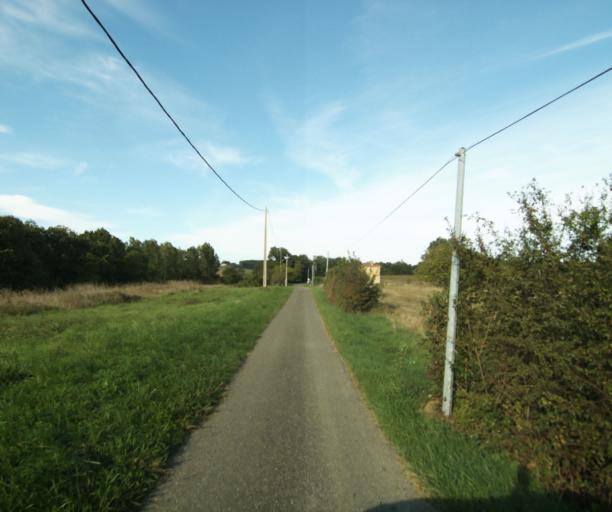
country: FR
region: Midi-Pyrenees
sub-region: Departement du Gers
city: Eauze
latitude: 43.8568
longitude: 0.0403
